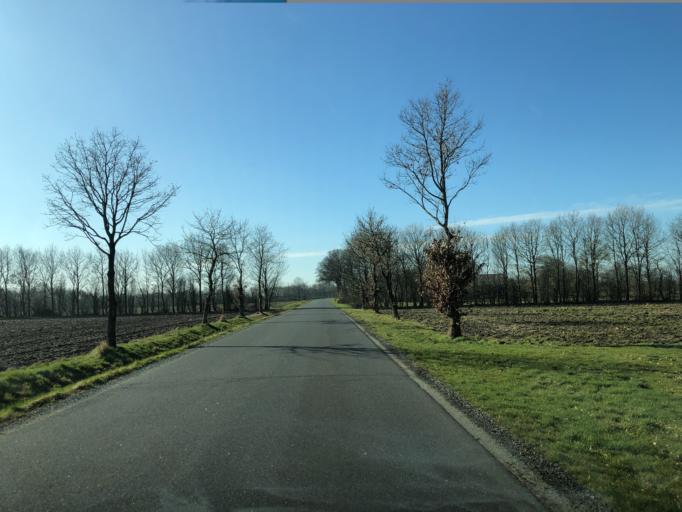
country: DK
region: Central Jutland
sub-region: Ikast-Brande Kommune
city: Bording Kirkeby
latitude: 56.1542
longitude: 9.3119
